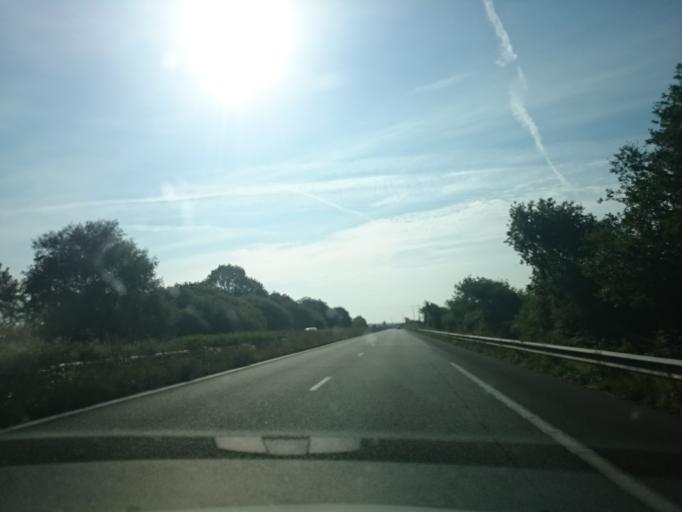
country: FR
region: Brittany
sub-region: Departement du Finistere
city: Pont-Aven
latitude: 47.8858
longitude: -3.7599
